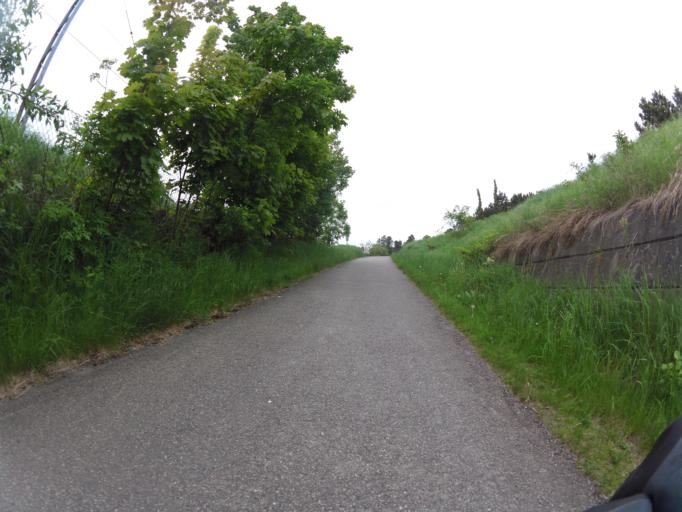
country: NO
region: Ostfold
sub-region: Moss
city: Moss
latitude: 59.4161
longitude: 10.6578
